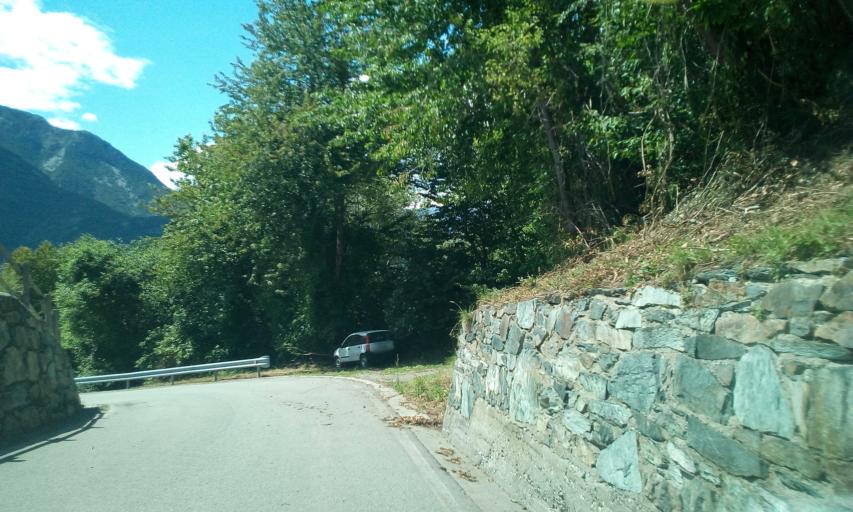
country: IT
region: Aosta Valley
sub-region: Valle d'Aosta
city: Berriat
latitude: 45.7035
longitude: 7.6919
